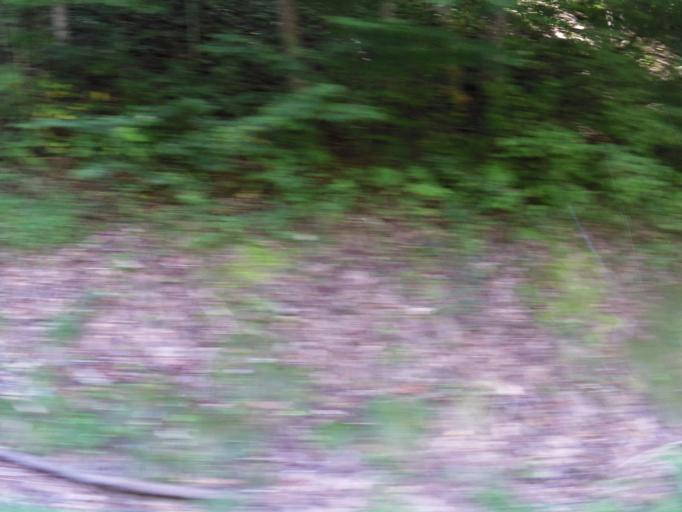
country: US
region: Kentucky
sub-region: Leslie County
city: Hyden
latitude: 37.1545
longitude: -83.4928
